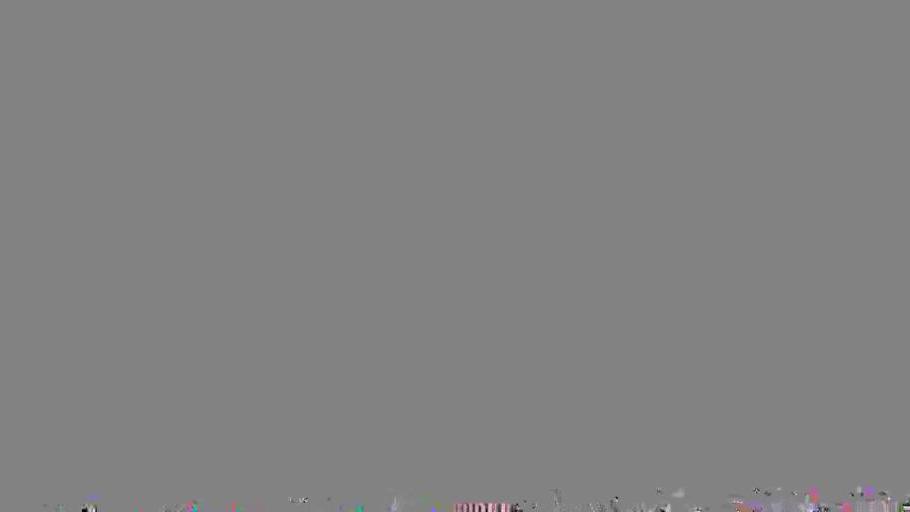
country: TH
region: Buriram
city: Chaloem Phra Kiat
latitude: 14.5470
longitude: 103.0105
